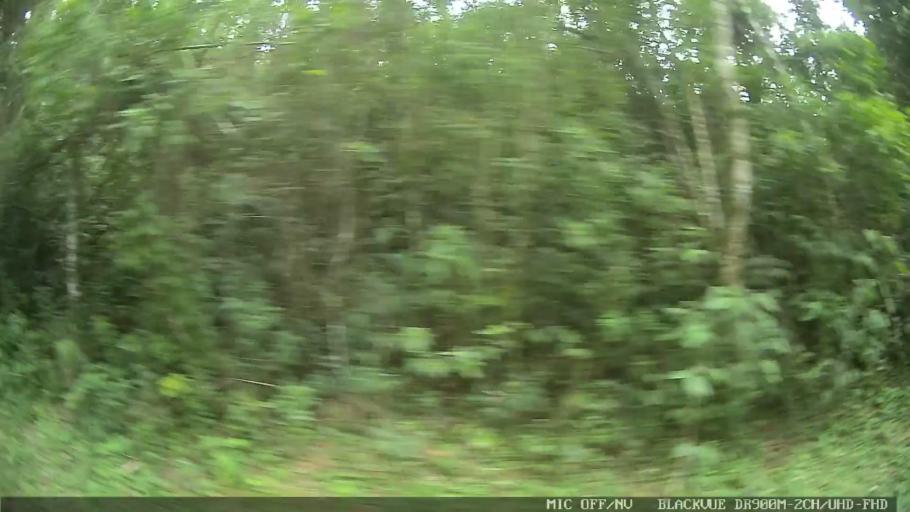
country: BR
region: Sao Paulo
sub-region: Caraguatatuba
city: Caraguatatuba
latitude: -23.5522
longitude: -45.6592
